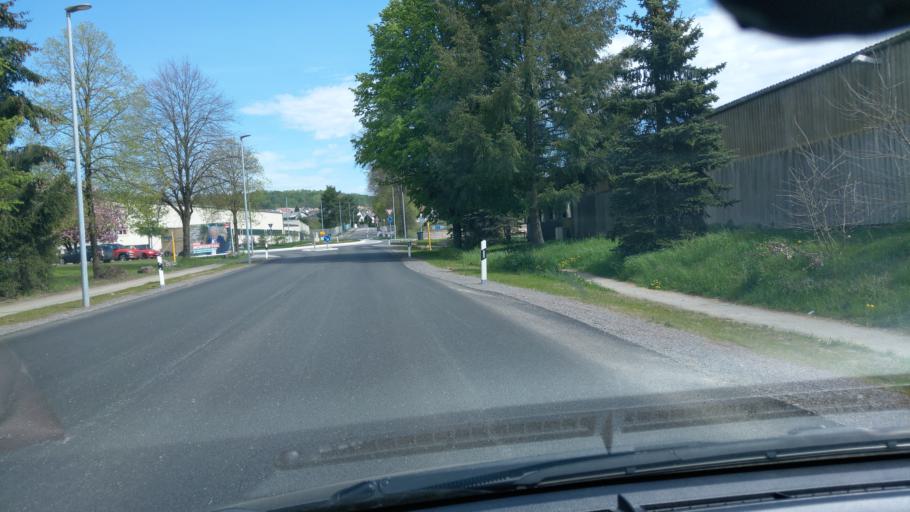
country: DE
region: Saarland
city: Spiesen-Elversberg
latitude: 49.3037
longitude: 7.1361
